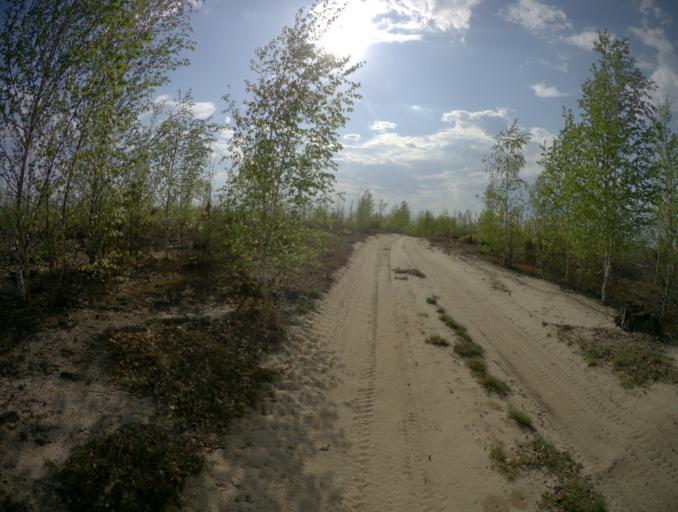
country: RU
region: Ivanovo
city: Talitsy
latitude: 56.4179
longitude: 42.2752
